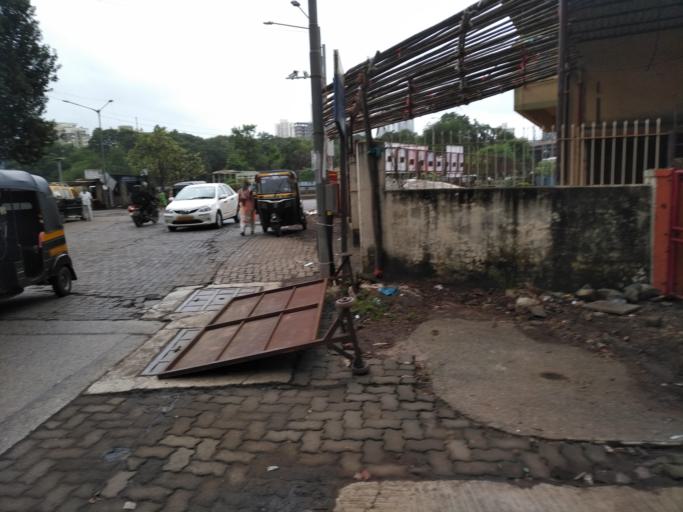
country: IN
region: Maharashtra
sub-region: Mumbai Suburban
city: Borivli
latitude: 19.2336
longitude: 72.8640
